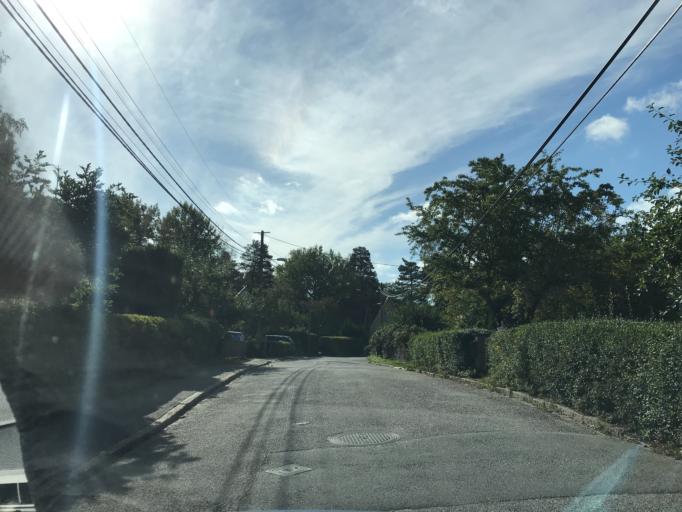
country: SE
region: Stockholm
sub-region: Huddinge Kommun
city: Segeltorp
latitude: 59.2787
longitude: 17.9669
